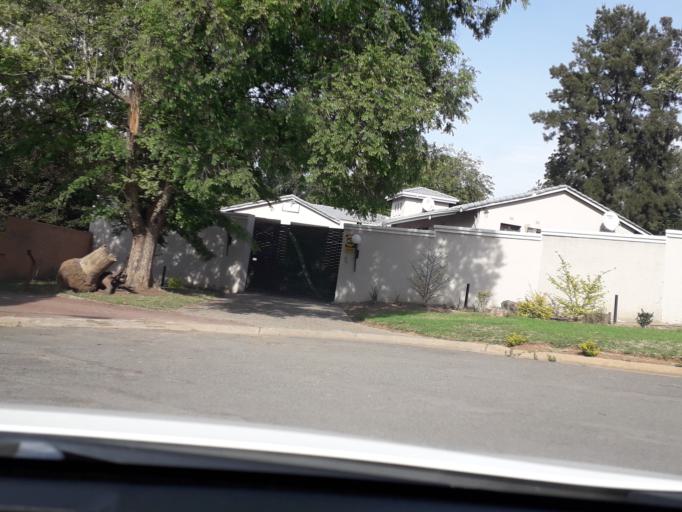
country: ZA
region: Gauteng
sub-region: City of Johannesburg Metropolitan Municipality
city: Modderfontein
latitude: -26.1208
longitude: 28.1090
